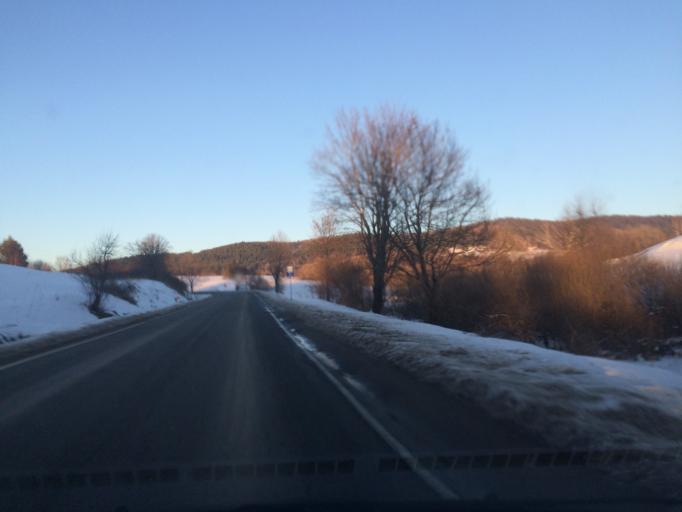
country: PL
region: Subcarpathian Voivodeship
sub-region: Powiat bieszczadzki
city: Czarna
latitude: 49.3267
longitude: 22.6695
